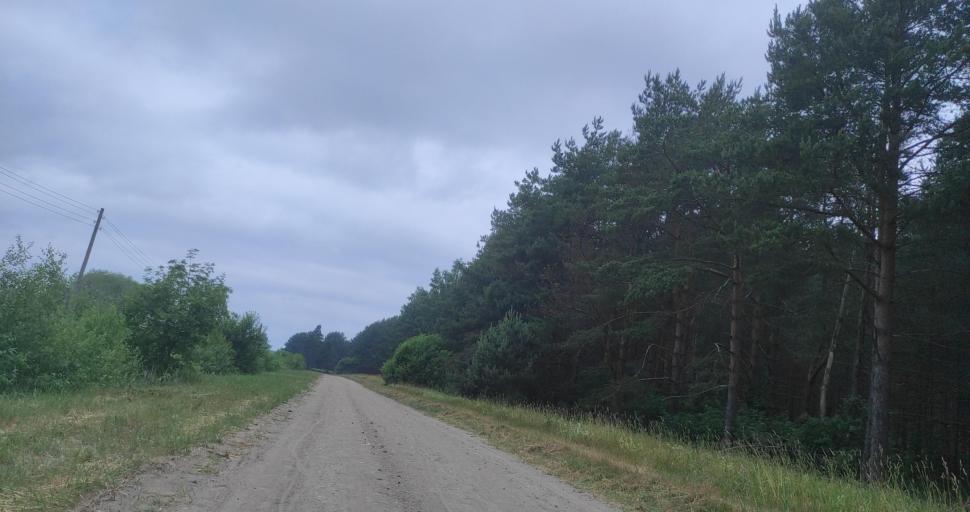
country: LV
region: Pavilostas
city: Pavilosta
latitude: 56.8860
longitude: 21.2006
